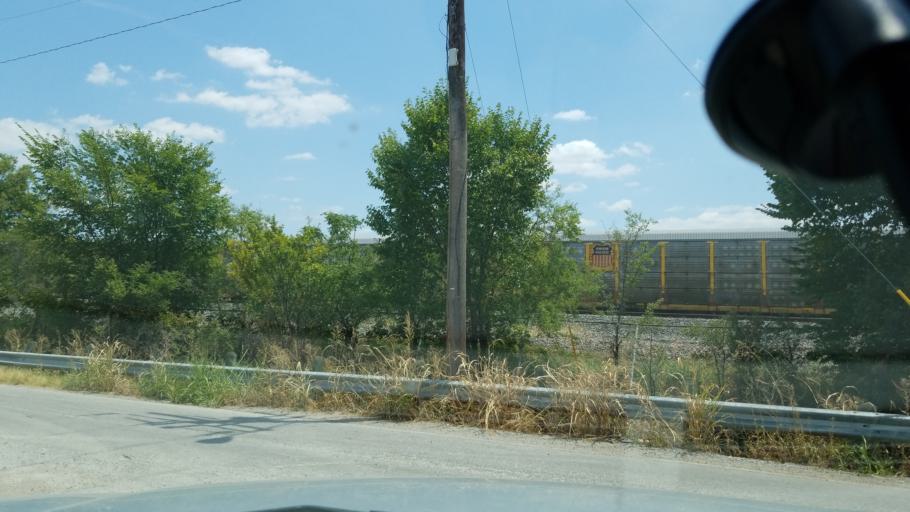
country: US
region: Texas
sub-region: Dallas County
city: Grand Prairie
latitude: 32.7463
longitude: -96.9771
